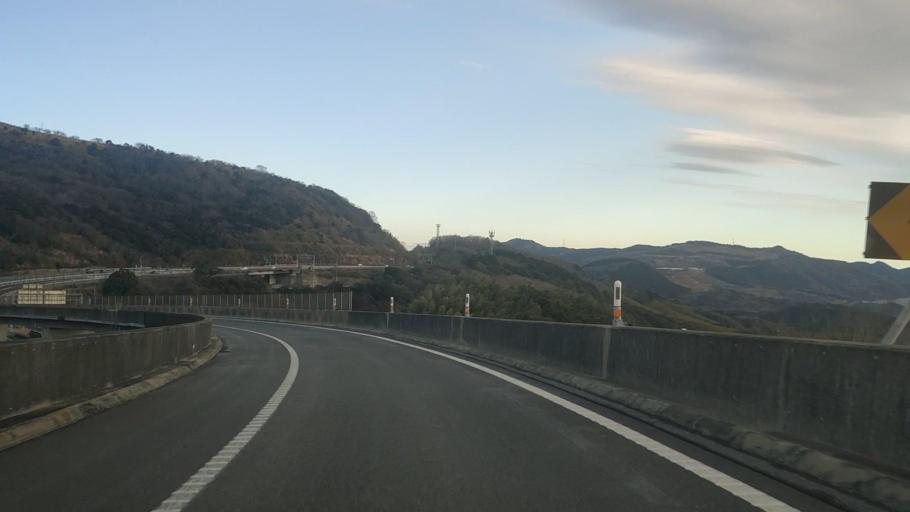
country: JP
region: Oita
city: Hiji
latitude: 33.3528
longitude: 131.4465
